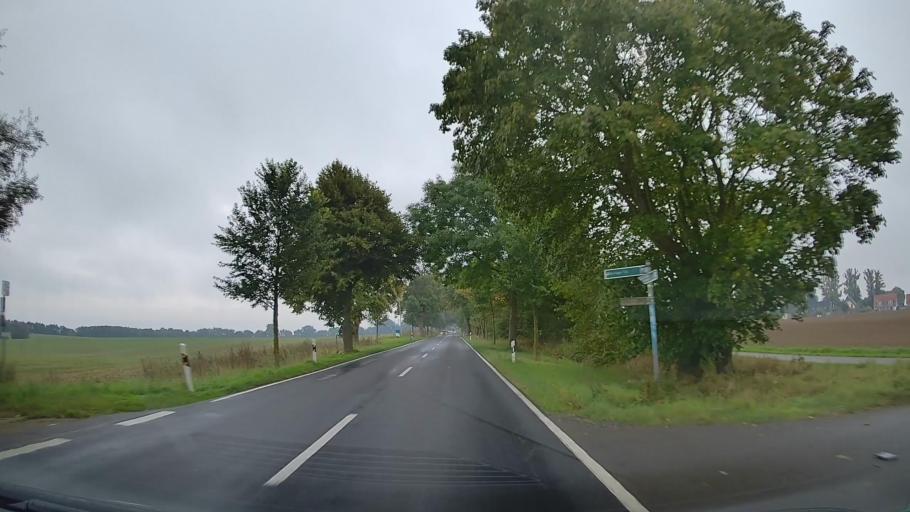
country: DE
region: Mecklenburg-Vorpommern
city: Ostseebad Boltenhagen
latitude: 53.9470
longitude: 11.2345
